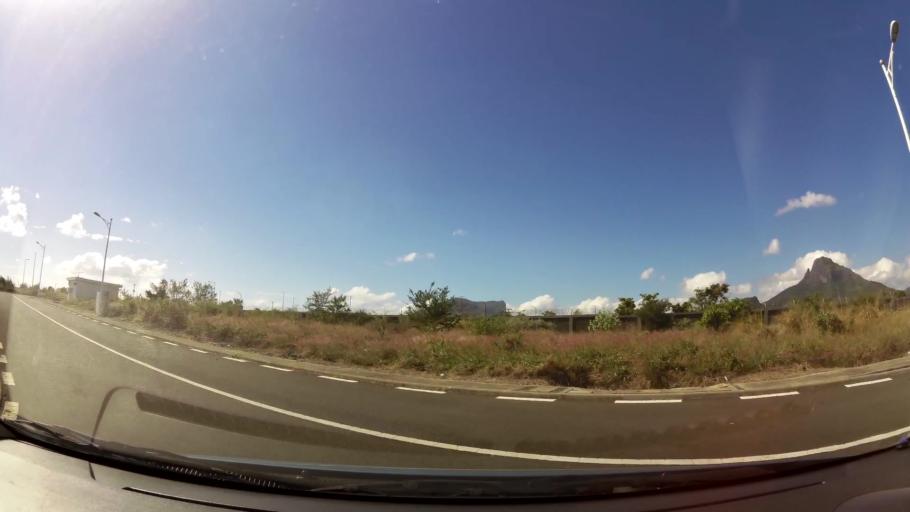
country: MU
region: Black River
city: Flic en Flac
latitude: -20.2786
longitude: 57.3854
